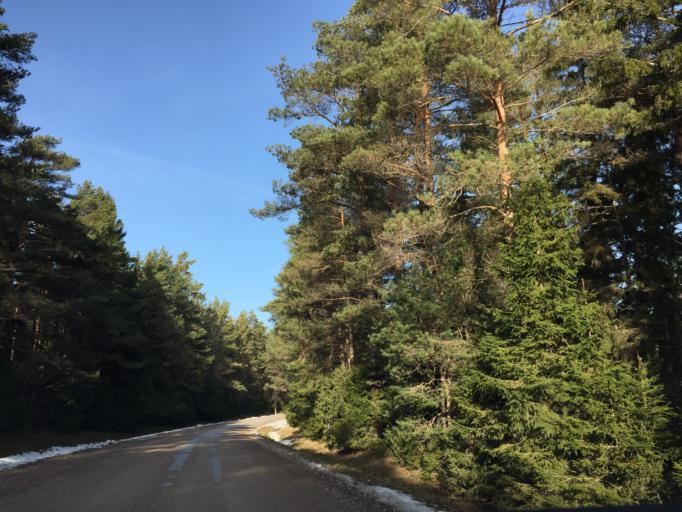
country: EE
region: Saare
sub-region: Kuressaare linn
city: Kuressaare
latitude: 58.3756
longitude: 22.0153
